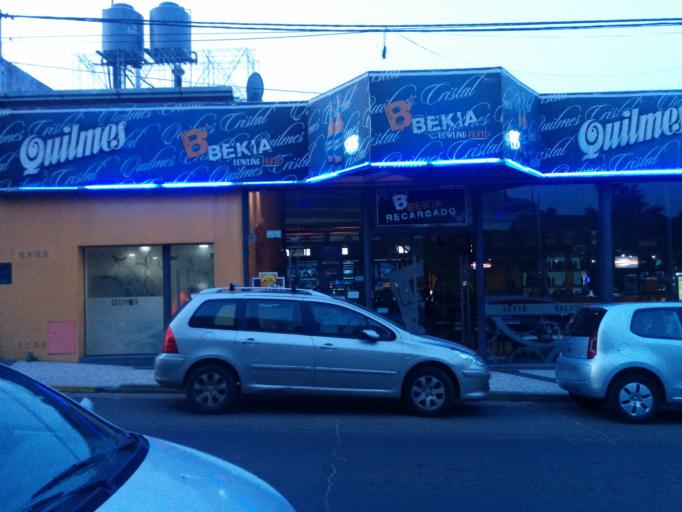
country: AR
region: Entre Rios
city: Concordia
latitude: -31.3935
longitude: -58.0163
